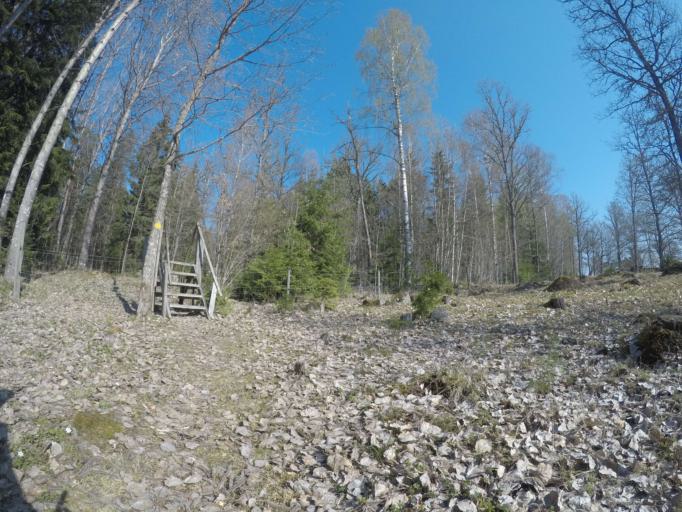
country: SE
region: Vaestmanland
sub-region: Hallstahammars Kommun
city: Kolback
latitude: 59.5351
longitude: 16.2813
